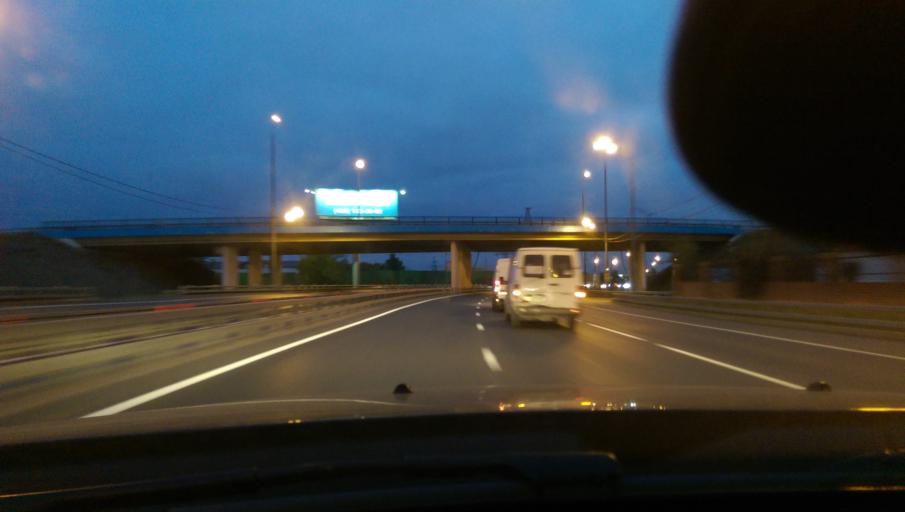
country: RU
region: Moscow
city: Vatutino
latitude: 55.9126
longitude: 37.6701
